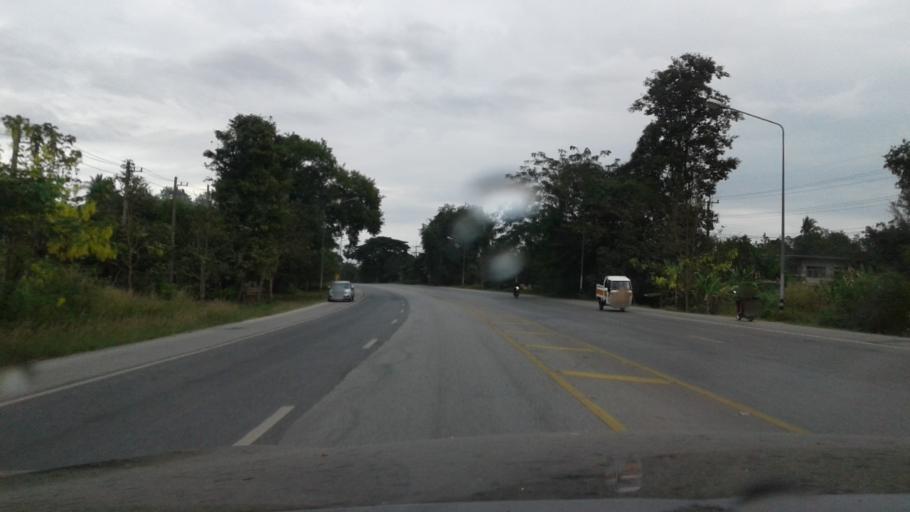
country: TH
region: Changwat Udon Thani
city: Nong Wua So
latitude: 17.2454
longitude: 102.5528
